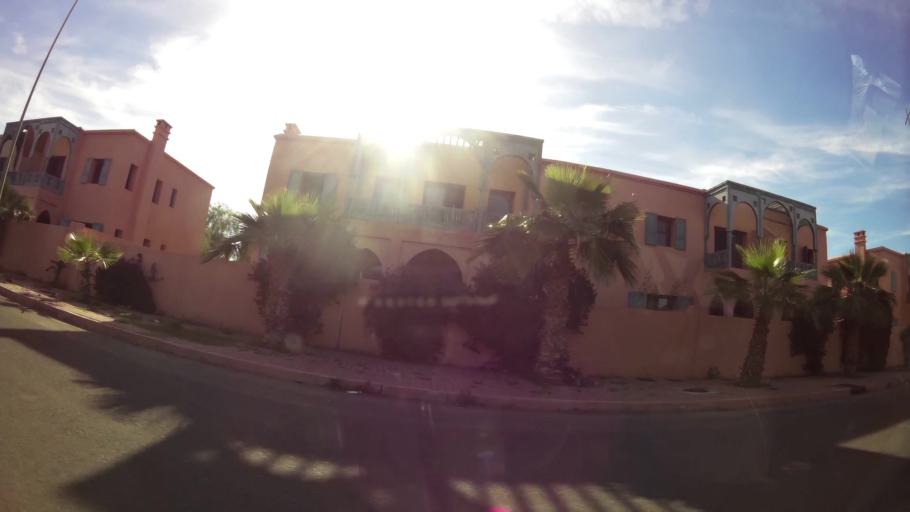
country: MA
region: Marrakech-Tensift-Al Haouz
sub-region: Marrakech
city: Marrakesh
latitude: 31.6761
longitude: -8.0517
